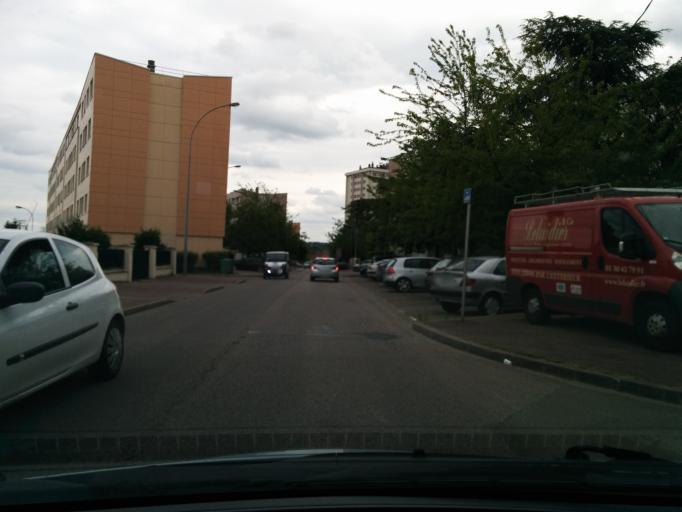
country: FR
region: Ile-de-France
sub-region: Departement des Yvelines
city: Mantes-la-Ville
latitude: 48.9786
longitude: 1.6999
